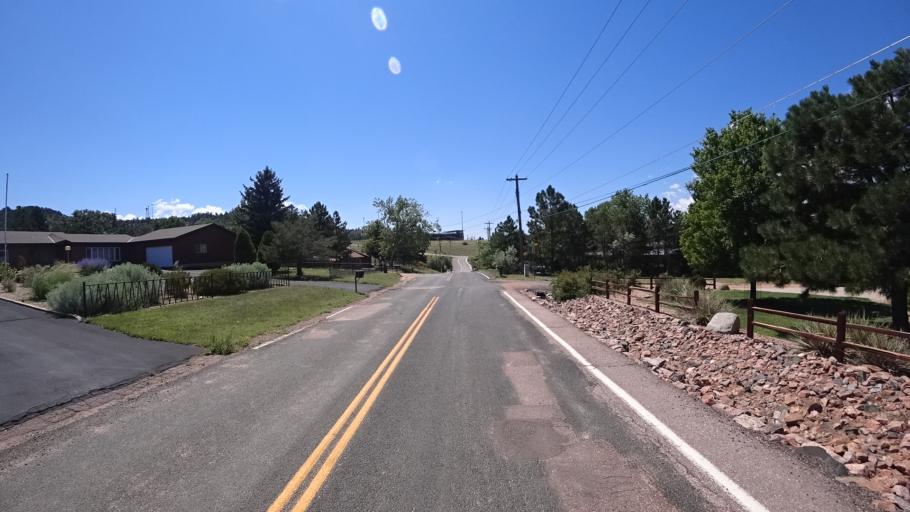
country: US
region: Colorado
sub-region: El Paso County
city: Colorado Springs
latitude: 38.9019
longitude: -104.8089
